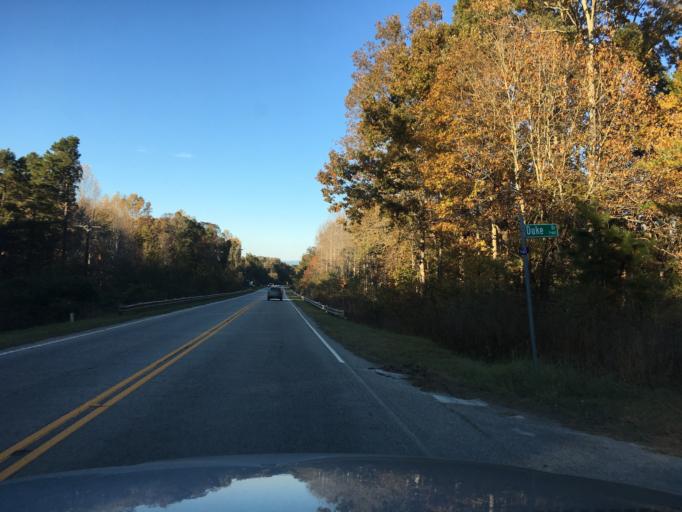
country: US
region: South Carolina
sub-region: Oconee County
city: Utica
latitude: 34.7153
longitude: -82.9228
